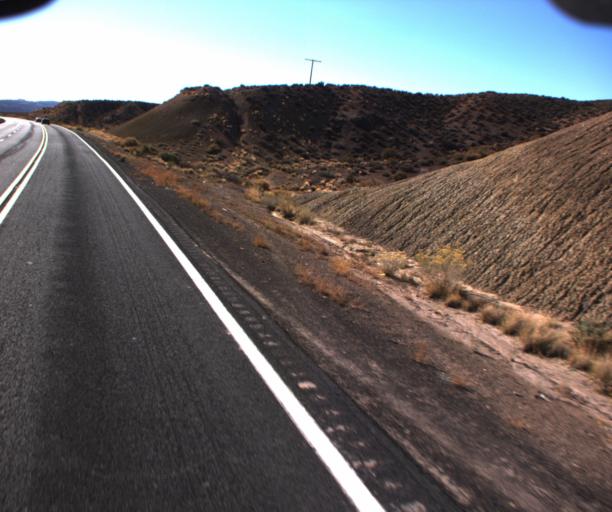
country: US
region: Arizona
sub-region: Coconino County
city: Tuba City
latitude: 36.2469
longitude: -111.4172
